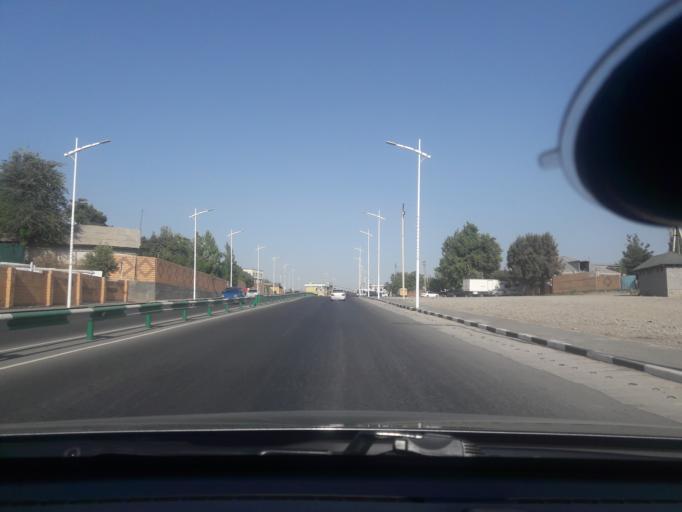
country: TJ
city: Shahrinav
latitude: 38.5763
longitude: 68.3273
